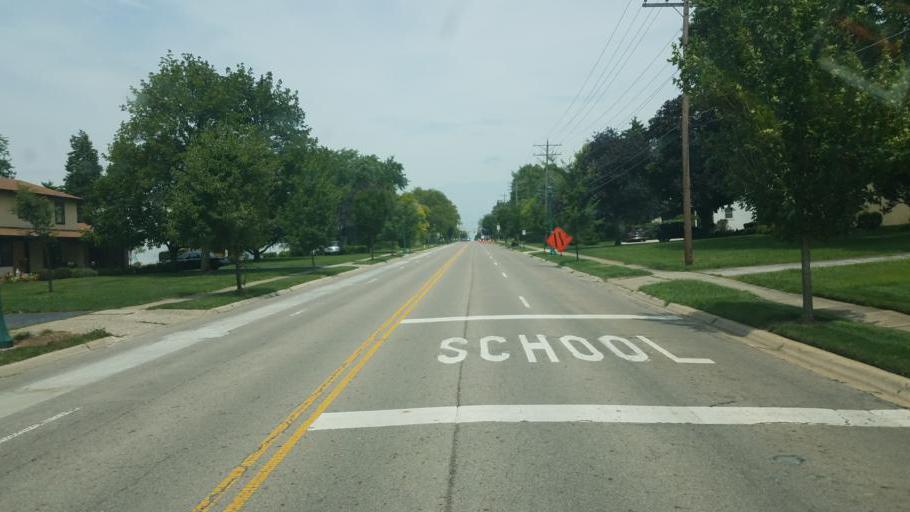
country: US
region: Ohio
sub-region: Franklin County
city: Upper Arlington
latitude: 40.0363
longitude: -83.0666
